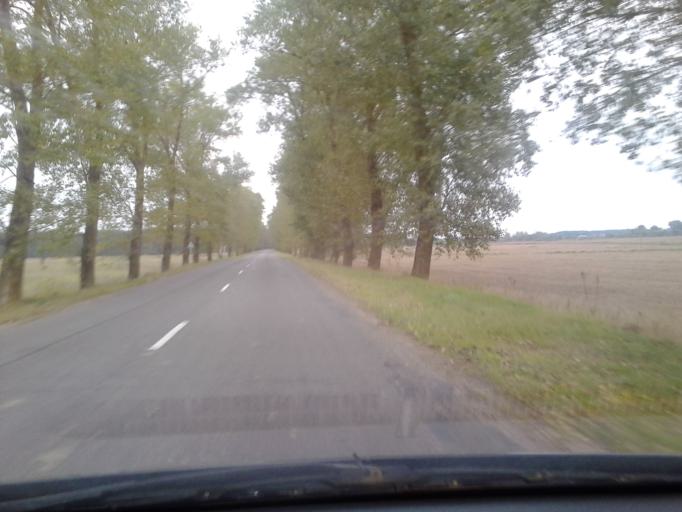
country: BY
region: Vitebsk
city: Pastavy
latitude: 55.1519
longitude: 26.9706
